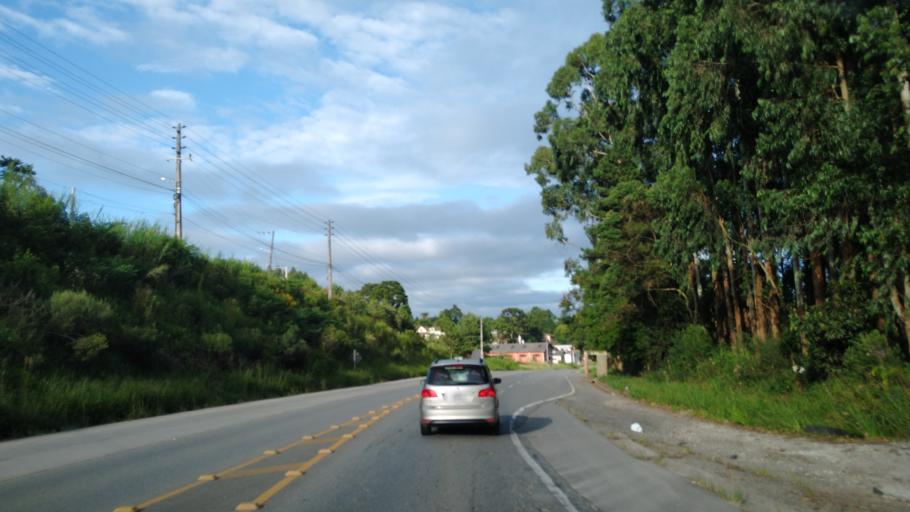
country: BR
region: Santa Catarina
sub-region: Sao Bento Do Sul
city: Sao Bento do Sul
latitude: -26.2374
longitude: -49.4283
